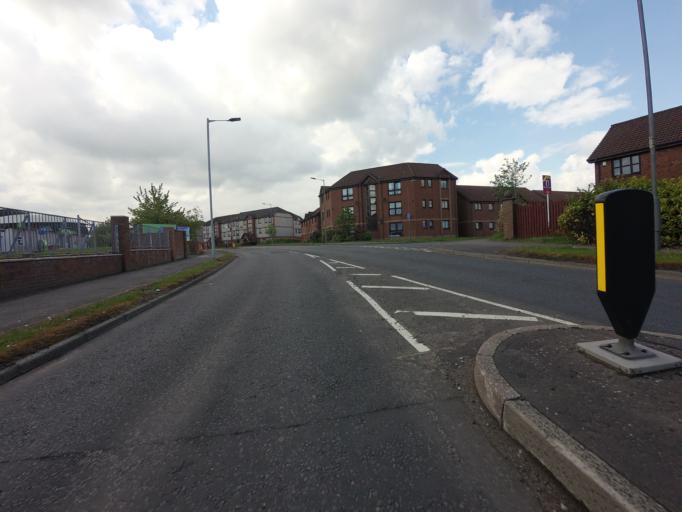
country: GB
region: Scotland
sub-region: Falkirk
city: Falkirk
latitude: 56.0173
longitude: -3.7932
